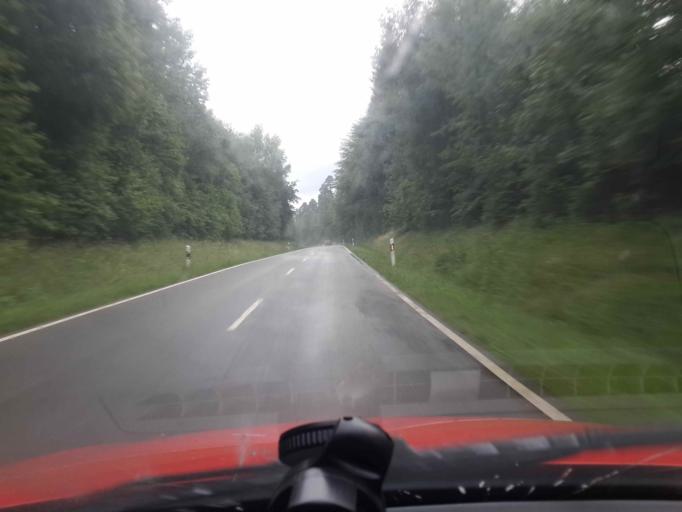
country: DE
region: Baden-Wuerttemberg
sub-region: Karlsruhe Region
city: Limbach
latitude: 49.4460
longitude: 9.2098
